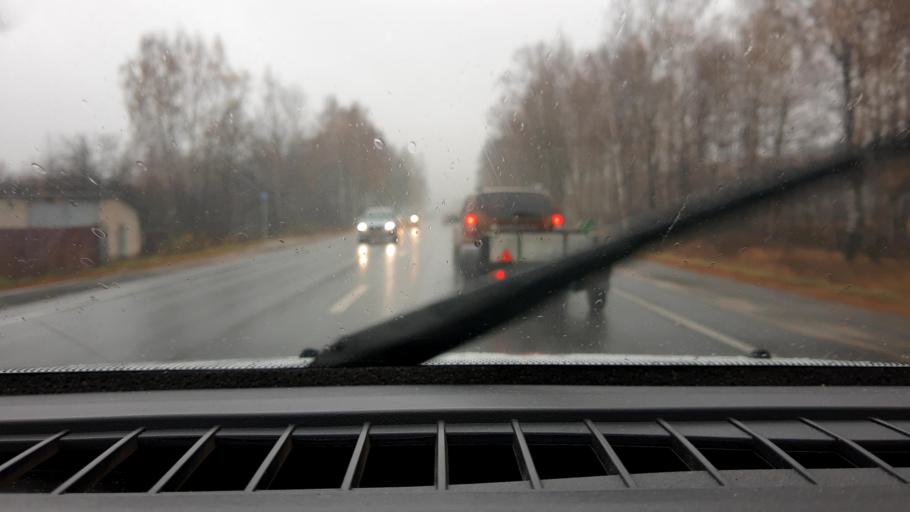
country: RU
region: Nizjnij Novgorod
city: Sitniki
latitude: 56.5313
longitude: 44.0237
